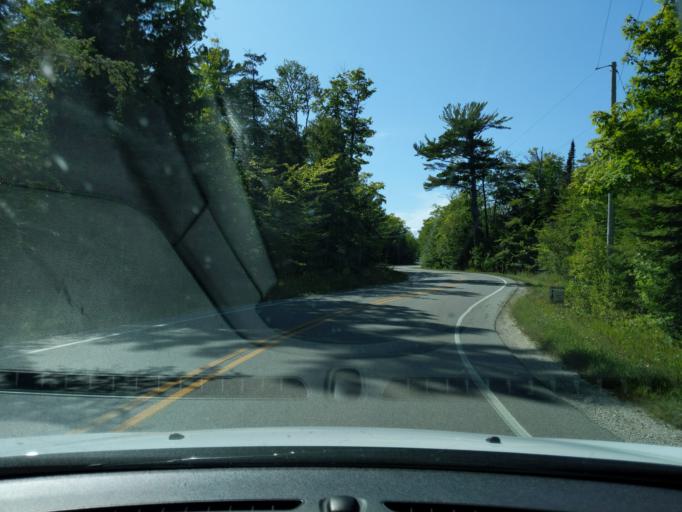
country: US
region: Michigan
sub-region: Delta County
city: Escanaba
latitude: 45.2893
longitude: -86.9846
